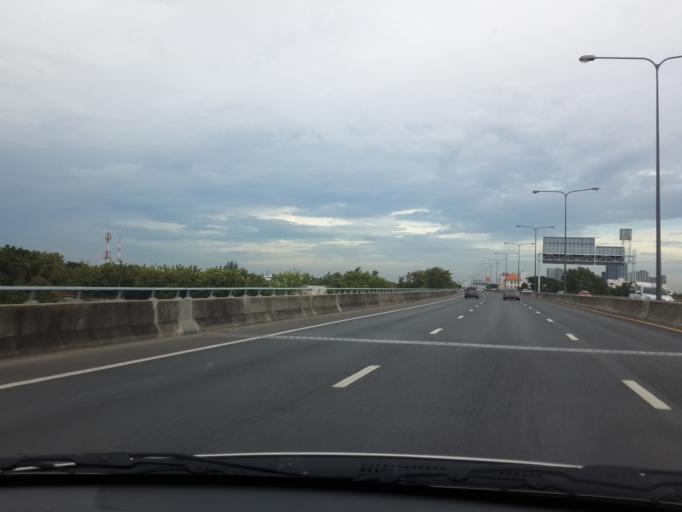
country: TH
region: Bangkok
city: Watthana
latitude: 13.7309
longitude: 100.6043
